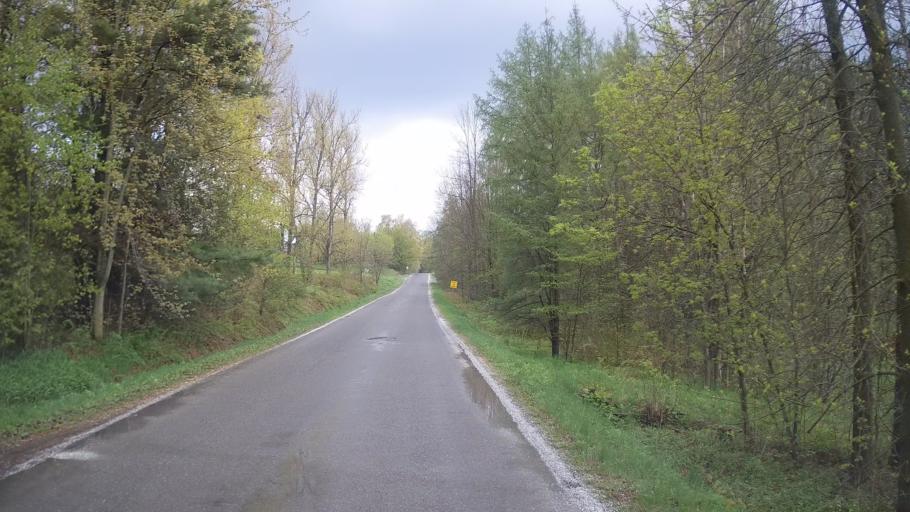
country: CA
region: Quebec
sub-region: Monteregie
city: Cowansville
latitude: 45.1819
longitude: -72.6950
